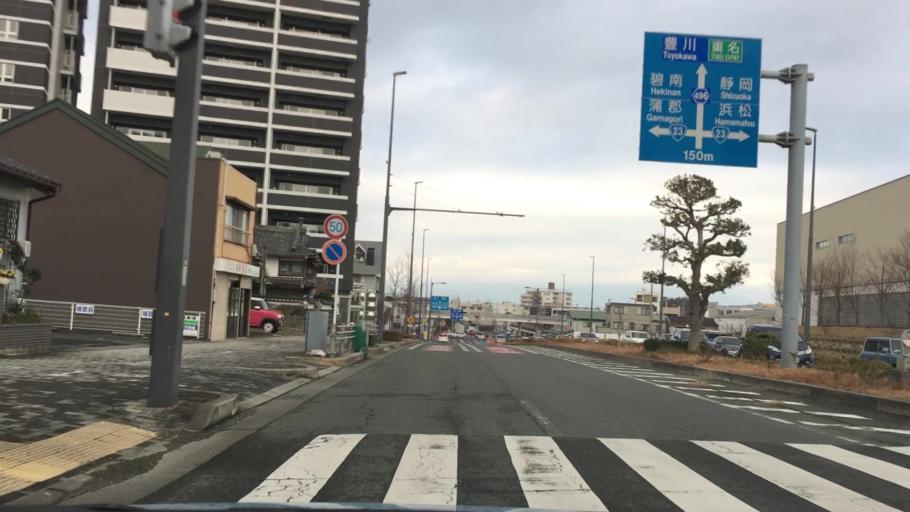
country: JP
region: Aichi
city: Toyohashi
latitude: 34.7676
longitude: 137.3829
